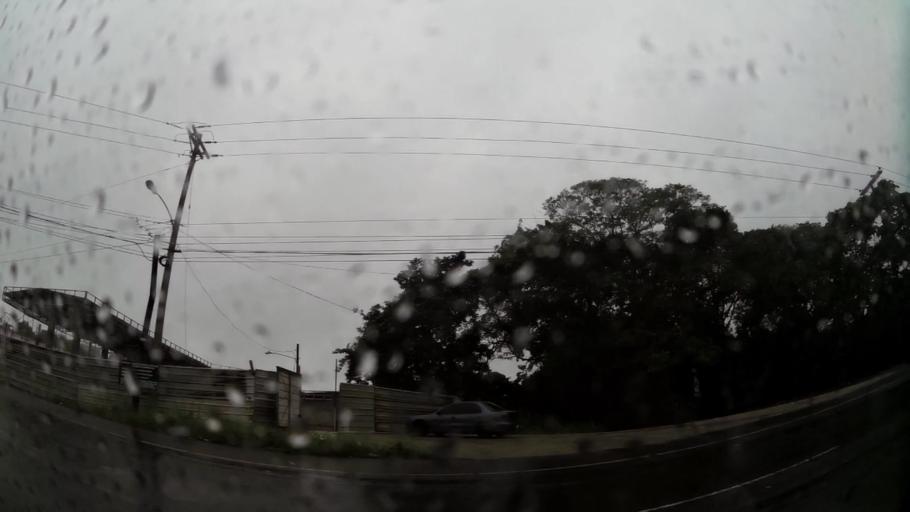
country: PA
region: Colon
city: Santa Rita Arriba
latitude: 9.3223
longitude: -79.7997
